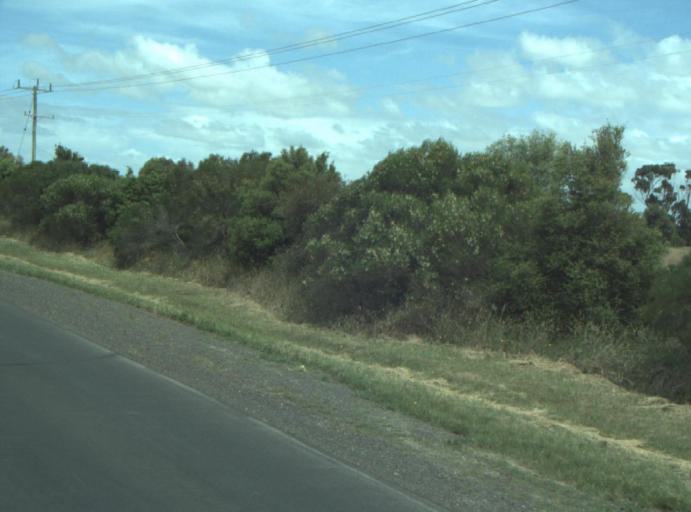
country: AU
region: Victoria
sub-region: Greater Geelong
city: Wandana Heights
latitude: -38.2430
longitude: 144.2963
